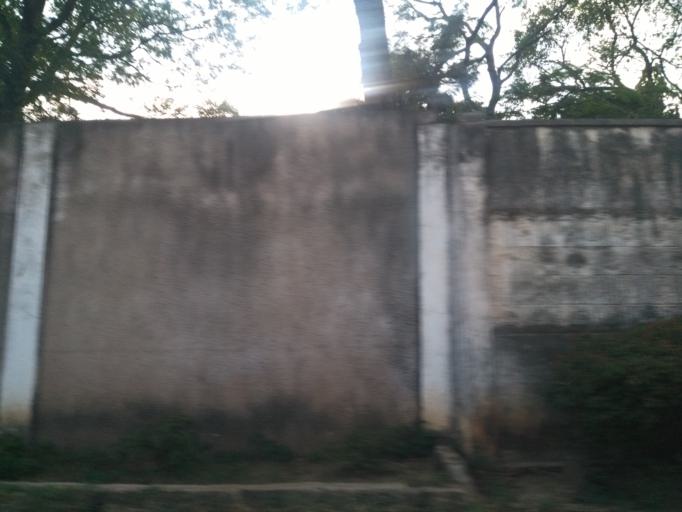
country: TZ
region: Dar es Salaam
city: Magomeni
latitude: -6.7861
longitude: 39.2724
